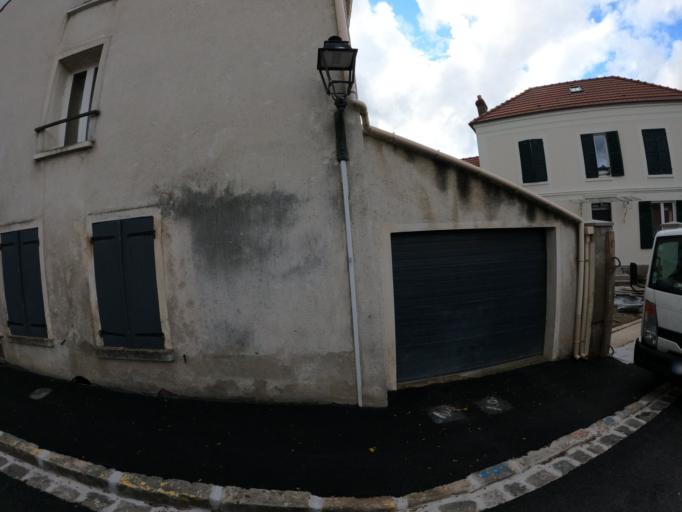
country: FR
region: Ile-de-France
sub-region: Departement de Seine-et-Marne
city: Coupvray
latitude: 48.8944
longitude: 2.7931
